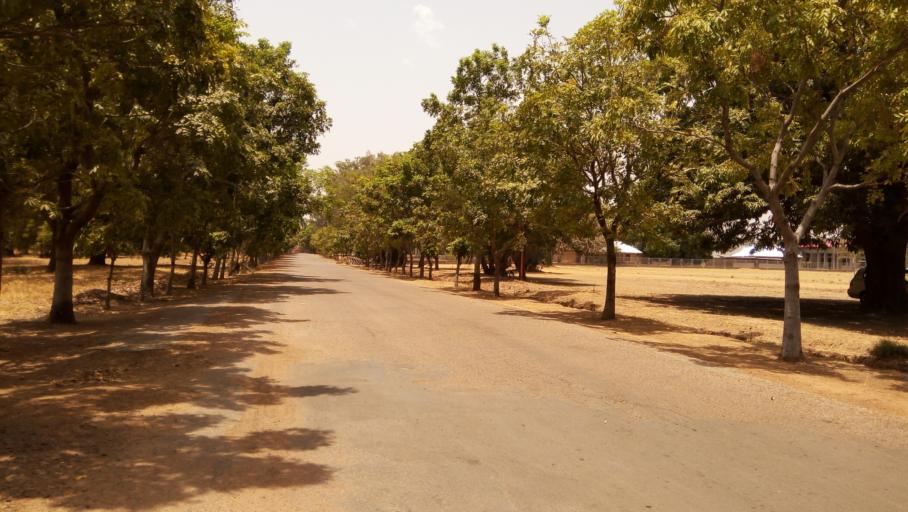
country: NG
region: Kaduna
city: Zaria
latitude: 11.1449
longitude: 7.6541
